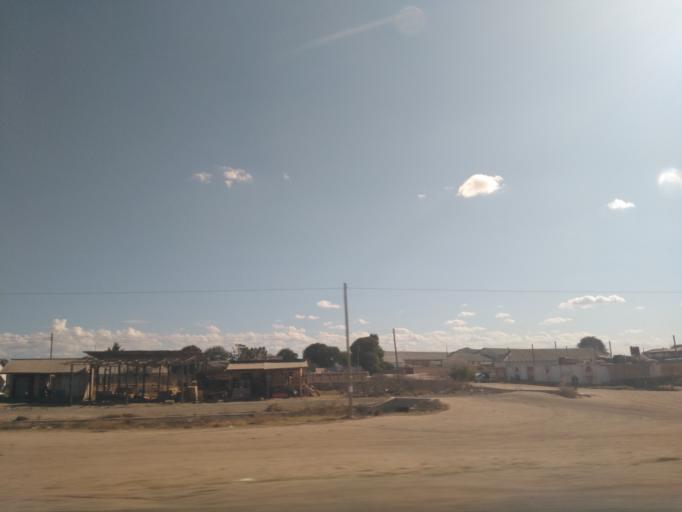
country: TZ
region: Dodoma
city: Dodoma
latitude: -6.1604
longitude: 35.7147
